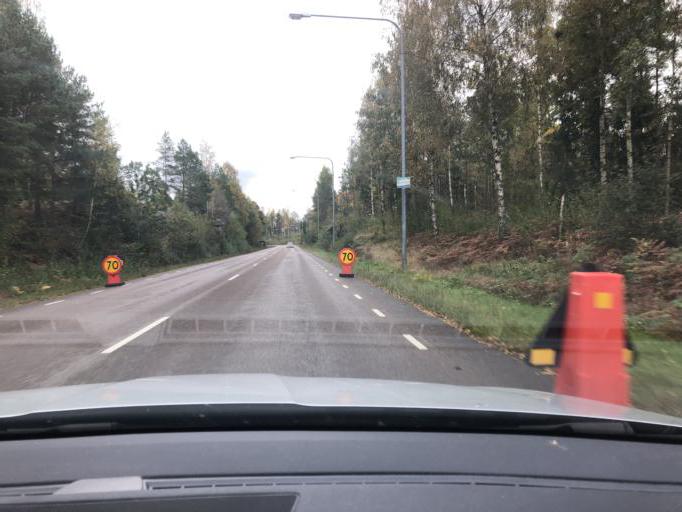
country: SE
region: Vaestra Goetaland
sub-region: Trollhattan
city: Trollhattan
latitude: 58.3138
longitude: 12.2733
